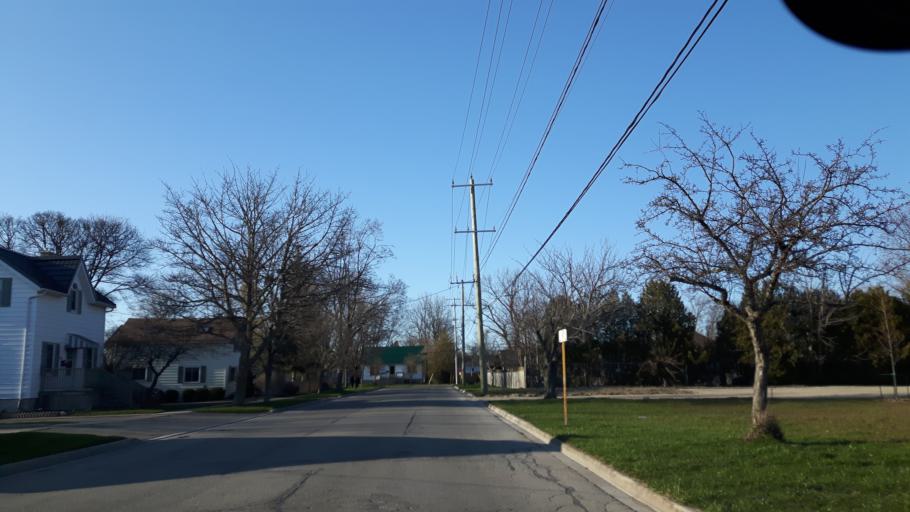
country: CA
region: Ontario
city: Goderich
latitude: 43.7381
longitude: -81.7164
